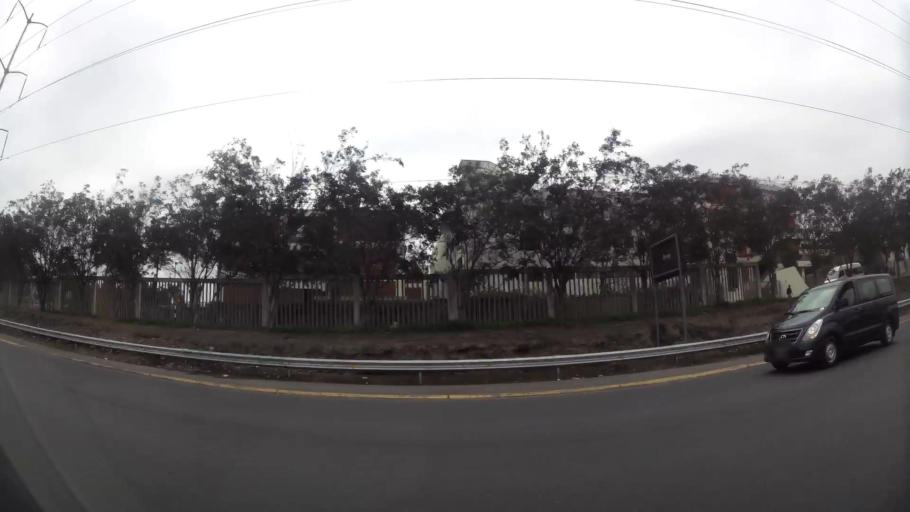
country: PE
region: Lima
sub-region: Lima
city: Surco
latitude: -12.1339
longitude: -76.9794
